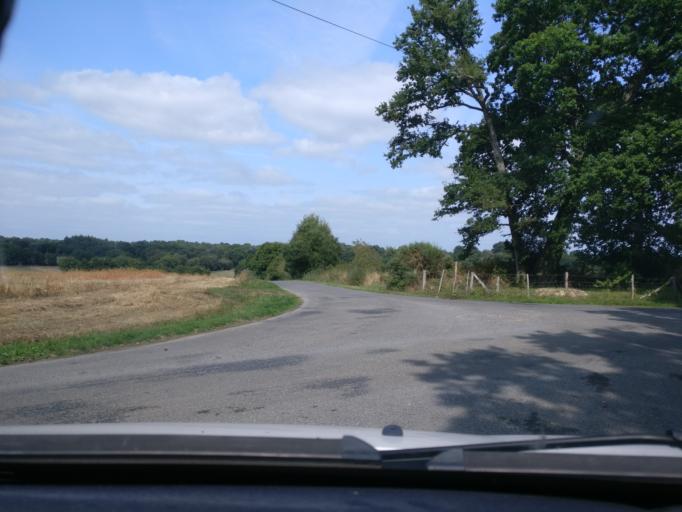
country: FR
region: Brittany
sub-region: Departement d'Ille-et-Vilaine
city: Gosne
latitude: 48.2634
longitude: -1.4841
